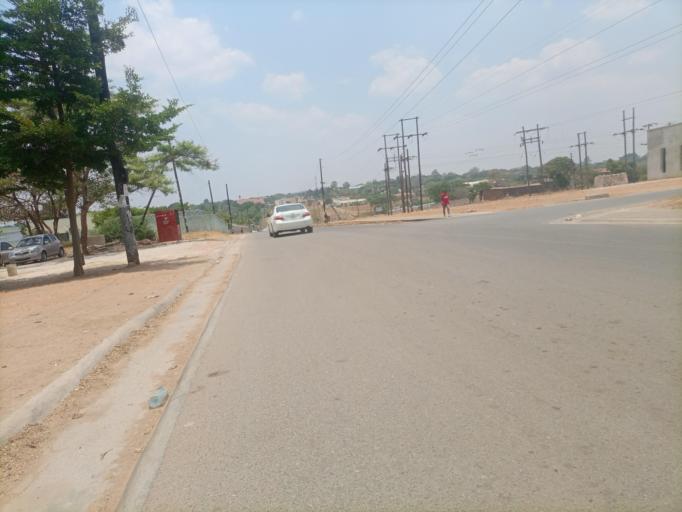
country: ZM
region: Lusaka
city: Lusaka
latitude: -15.4089
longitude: 28.3701
